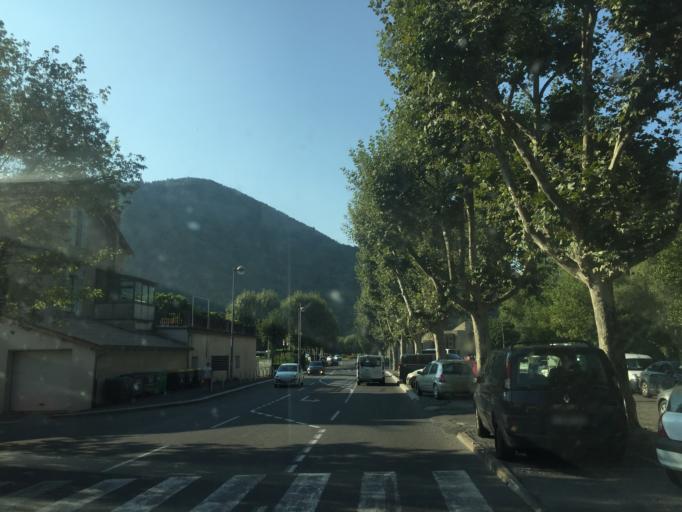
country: FR
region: Provence-Alpes-Cote d'Azur
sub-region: Departement des Alpes-de-Haute-Provence
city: Digne-les-Bains
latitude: 44.0930
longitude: 6.2306
